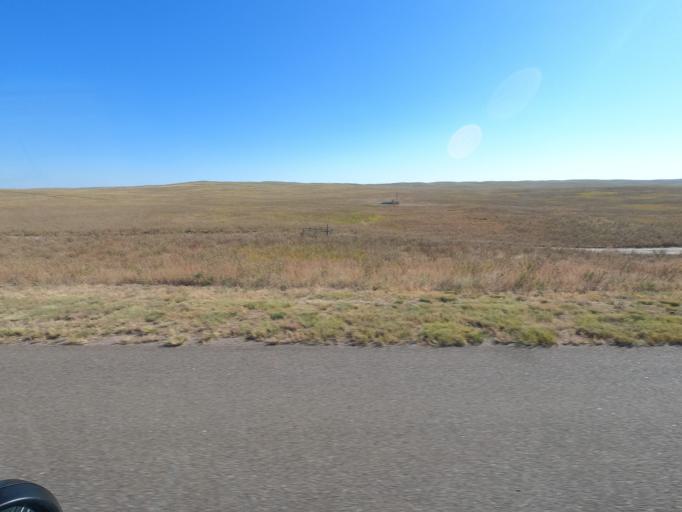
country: US
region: Nebraska
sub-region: Cheyenne County
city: Sidney
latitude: 40.8303
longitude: -102.7795
